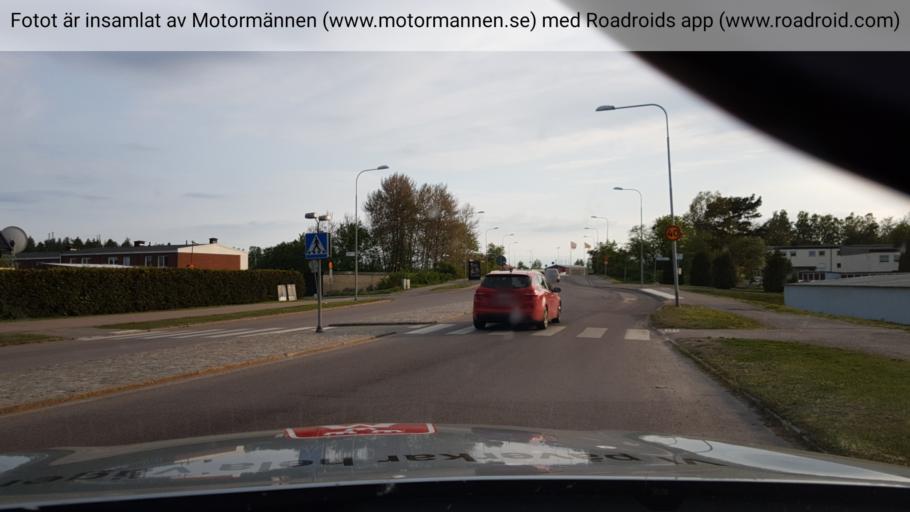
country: SE
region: Vaestmanland
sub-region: Vasteras
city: Vasteras
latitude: 59.5973
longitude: 16.5037
